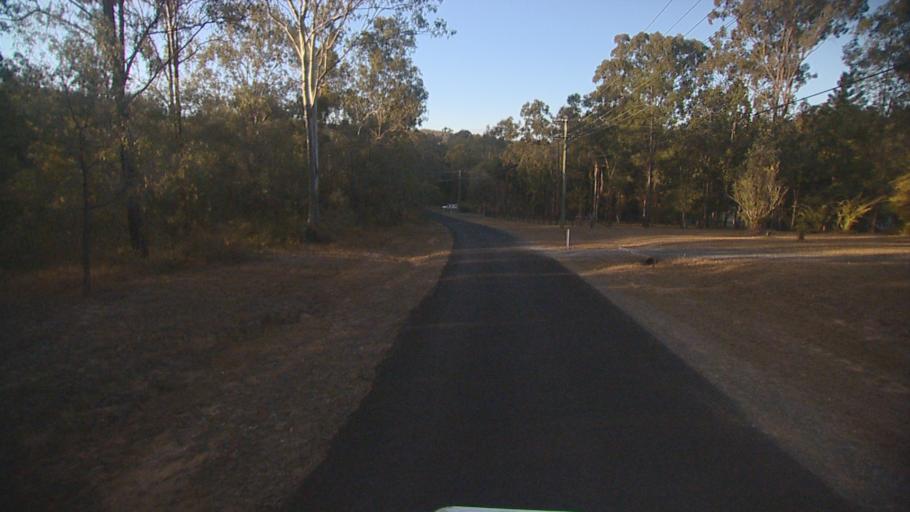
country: AU
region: Queensland
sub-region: Logan
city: Cedar Vale
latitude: -27.8479
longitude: 153.0818
